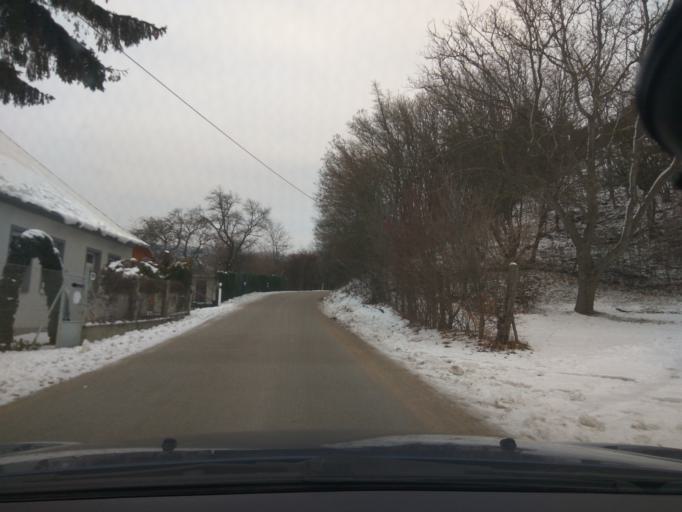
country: SK
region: Nitriansky
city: Stara Tura
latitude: 48.8205
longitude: 17.7044
